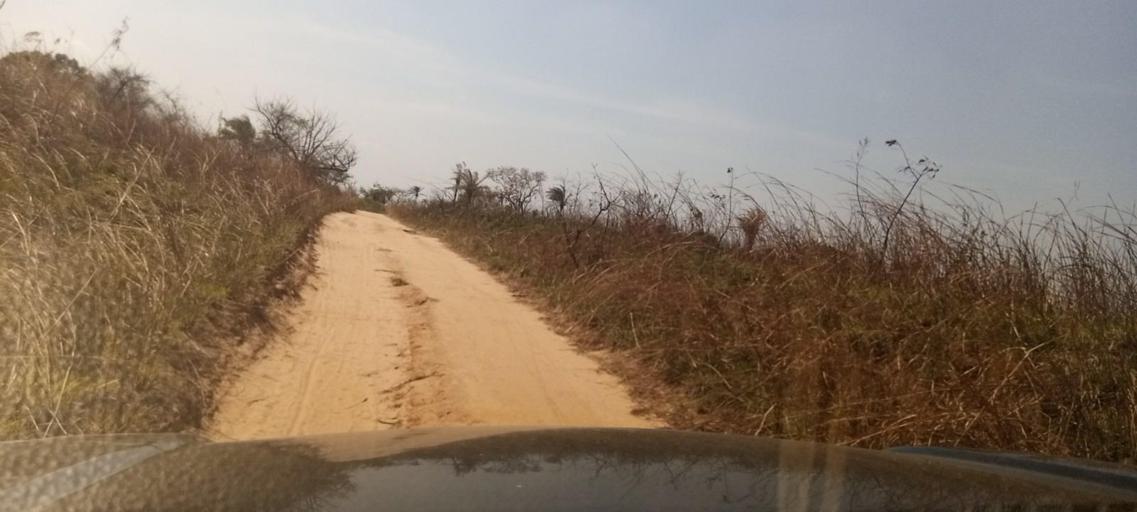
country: CD
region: Kasai-Oriental
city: Kabinda
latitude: -5.7970
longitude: 25.0299
